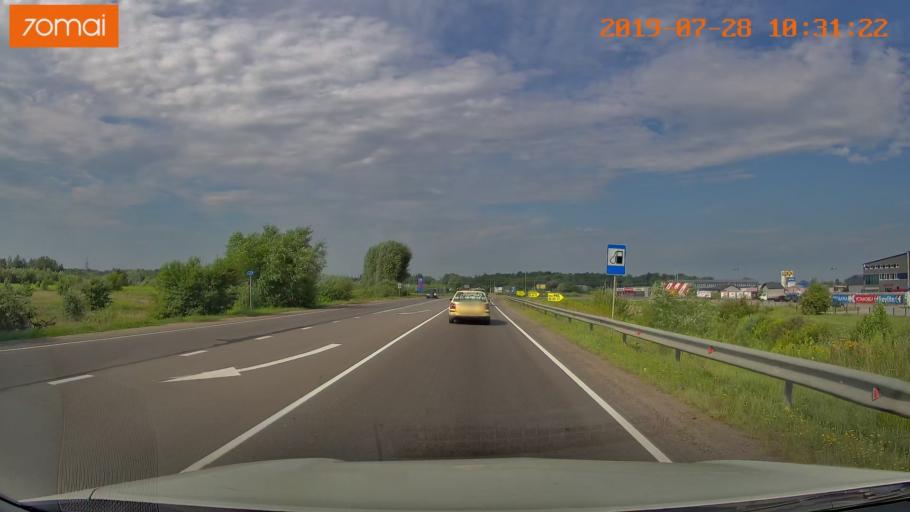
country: RU
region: Kaliningrad
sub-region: Gorod Kaliningrad
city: Kaliningrad
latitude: 54.7606
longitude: 20.4563
